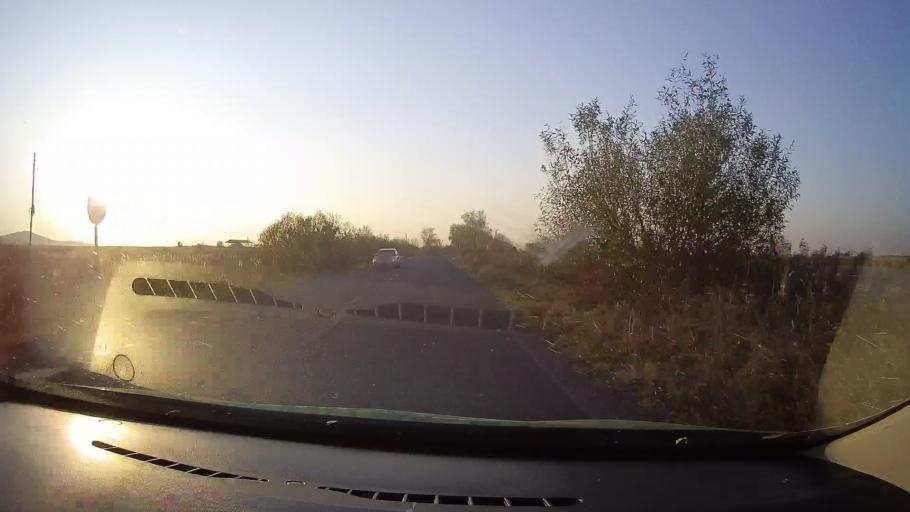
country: RO
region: Arad
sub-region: Comuna Bocsig
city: Bocsig
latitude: 46.4212
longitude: 21.9230
